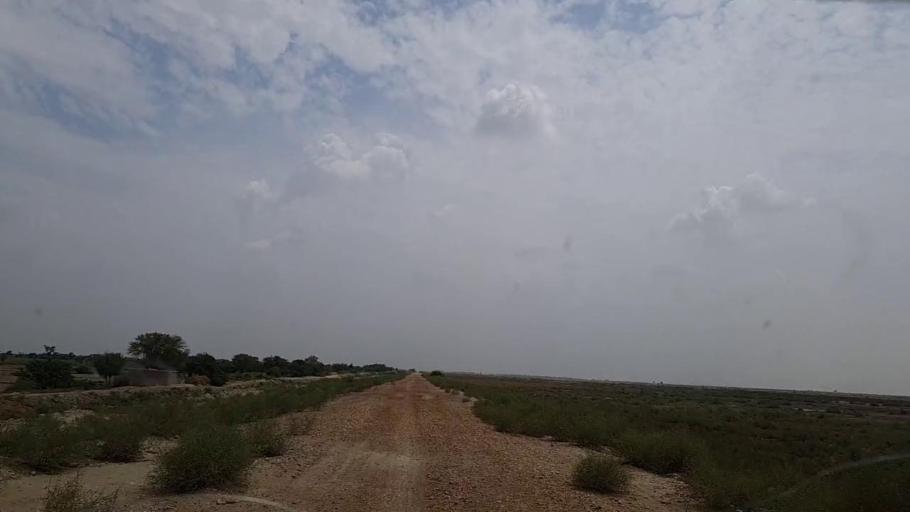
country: PK
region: Sindh
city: Johi
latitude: 26.7964
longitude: 67.6018
